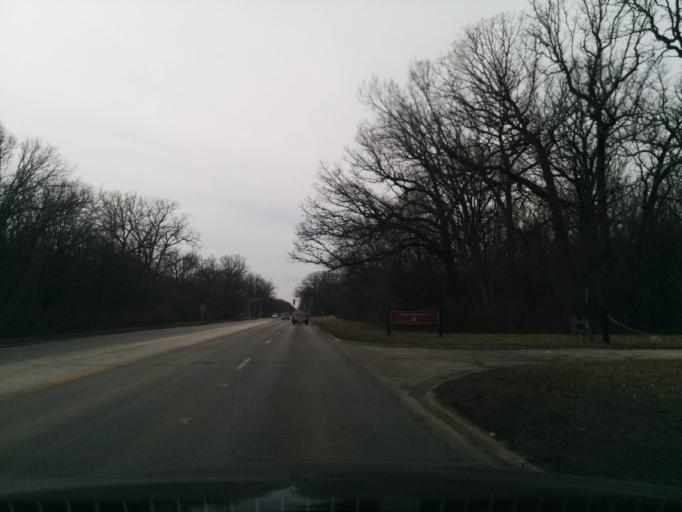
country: US
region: Illinois
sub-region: Cook County
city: La Grange Park
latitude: 41.8342
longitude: -87.8783
